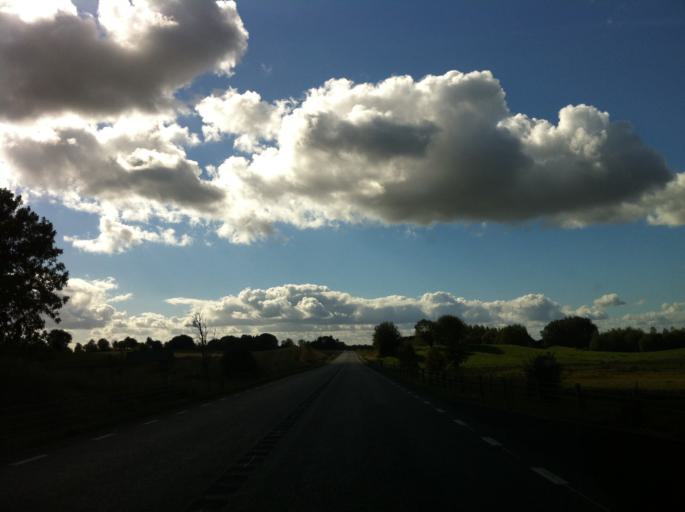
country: SE
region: Skane
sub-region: Tomelilla Kommun
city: Tomelilla
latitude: 55.6503
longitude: 14.0215
